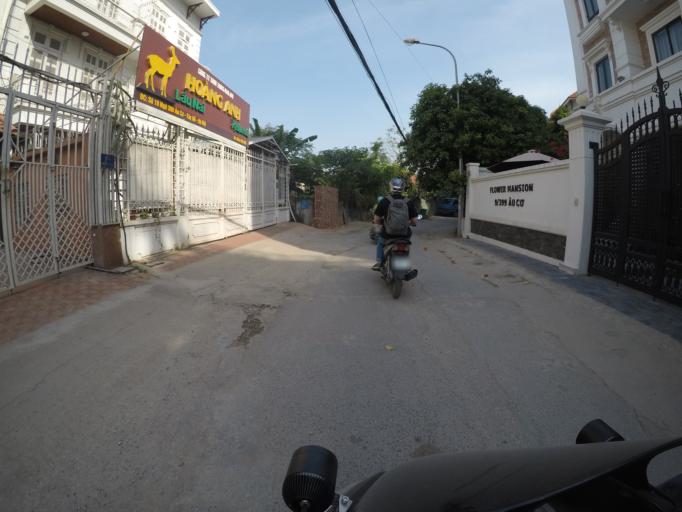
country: VN
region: Ha Noi
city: Tay Ho
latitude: 21.0750
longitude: 105.8215
